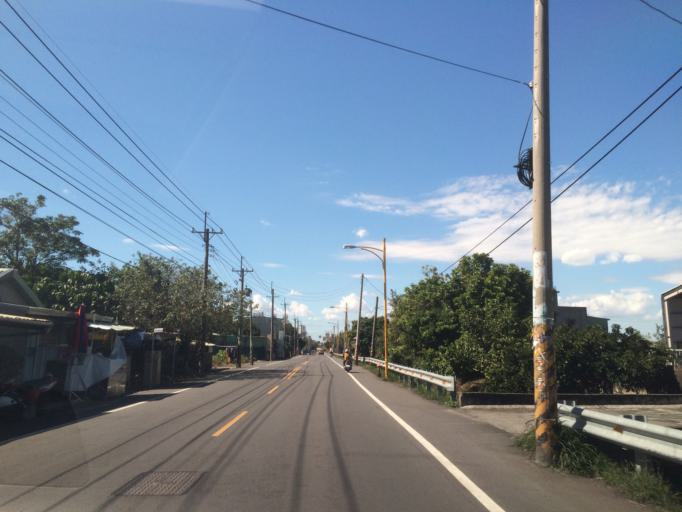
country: TW
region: Taiwan
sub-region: Yunlin
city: Douliu
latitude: 23.7032
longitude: 120.5648
